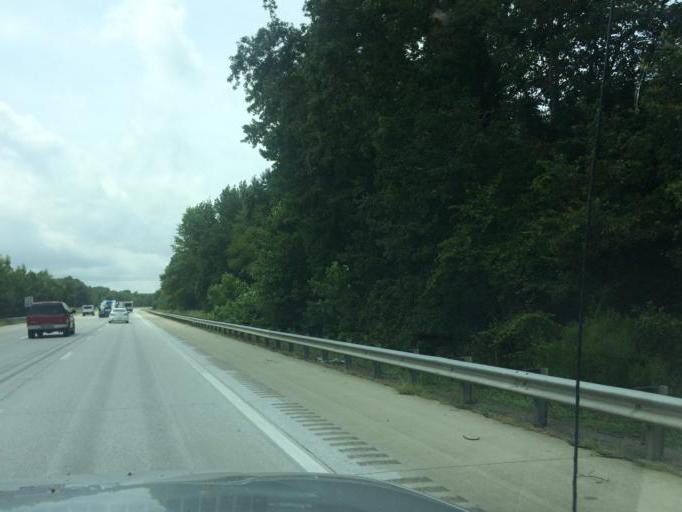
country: US
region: South Carolina
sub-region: Anderson County
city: Piedmont
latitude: 34.6889
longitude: -82.5109
